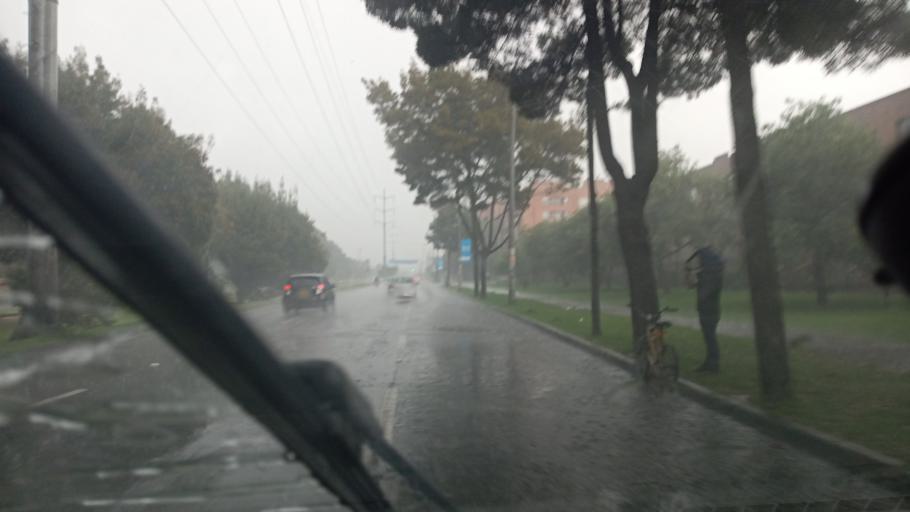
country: CO
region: Bogota D.C.
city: Bogota
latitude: 4.6682
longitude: -74.1331
